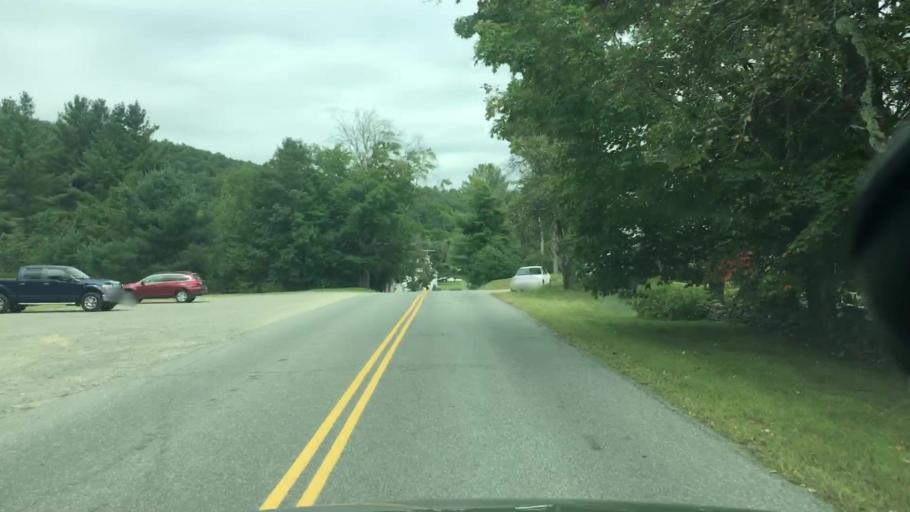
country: US
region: Massachusetts
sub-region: Franklin County
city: Colrain
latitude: 42.7847
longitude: -72.7683
